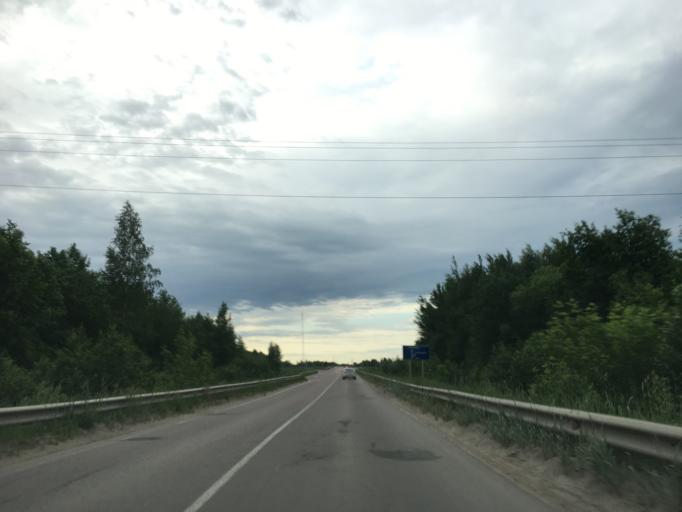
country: RU
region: Pskov
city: Pskov
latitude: 57.8547
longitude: 28.3069
